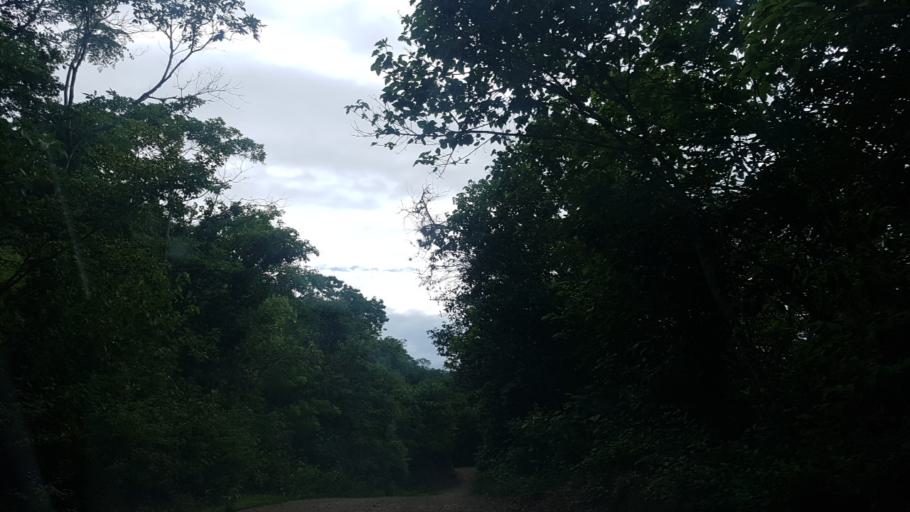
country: NI
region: Nueva Segovia
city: Ocotal
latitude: 13.5994
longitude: -86.4250
